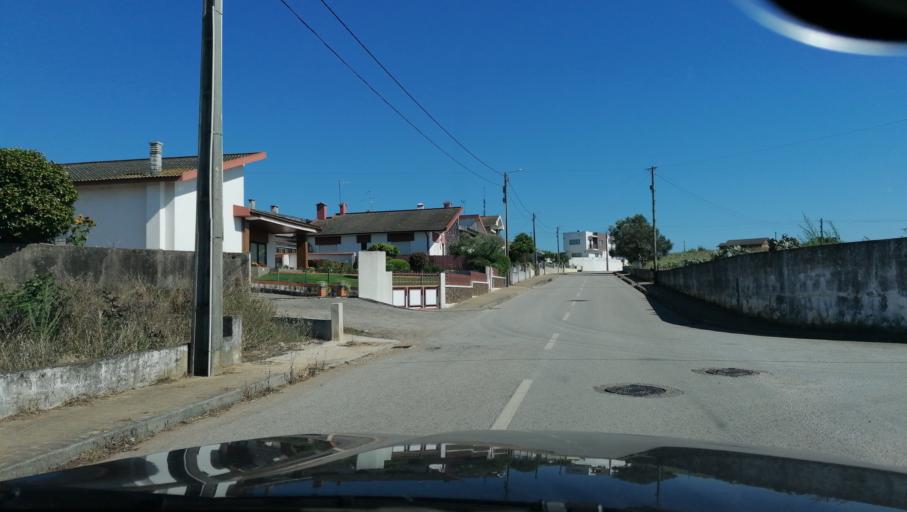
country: PT
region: Aveiro
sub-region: Estarreja
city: Salreu
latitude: 40.7458
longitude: -8.5472
